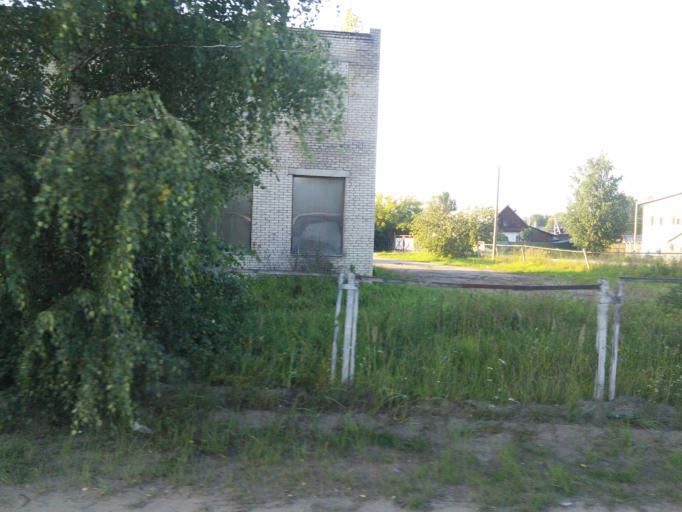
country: RU
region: Vologda
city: Chagoda
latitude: 59.1602
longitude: 35.3242
